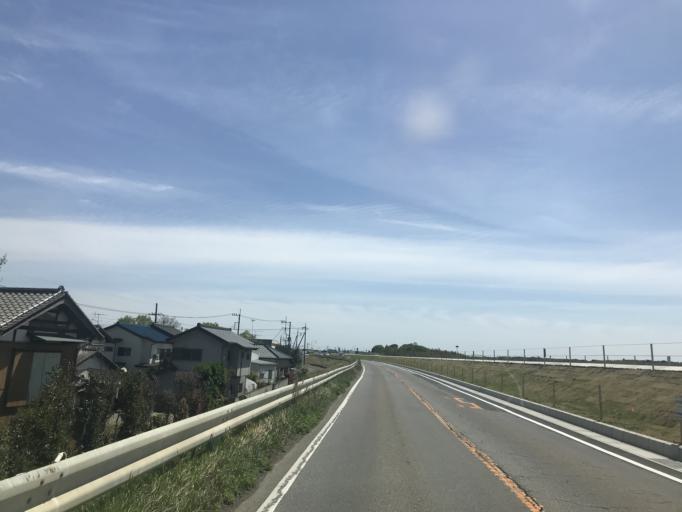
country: JP
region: Ibaraki
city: Ishige
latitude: 36.0718
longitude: 139.9797
